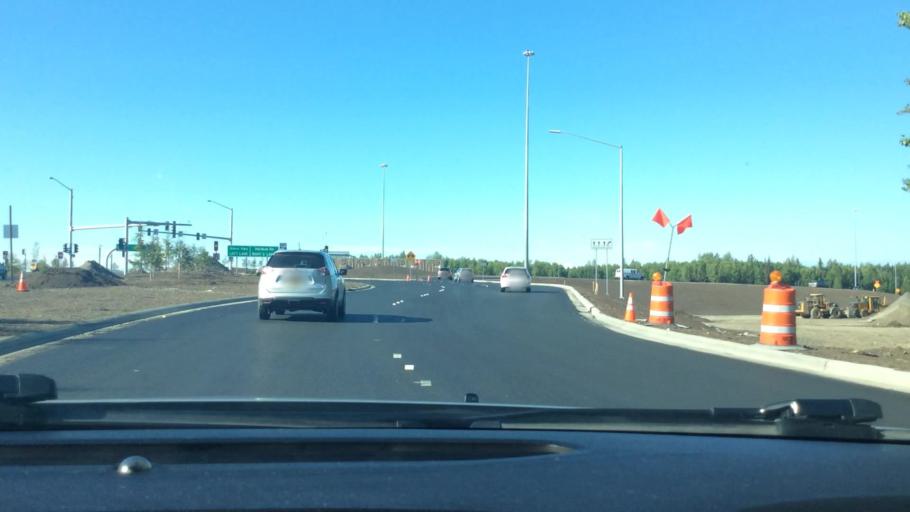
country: US
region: Alaska
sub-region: Anchorage Municipality
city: Elmendorf Air Force Base
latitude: 61.2247
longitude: -149.7335
